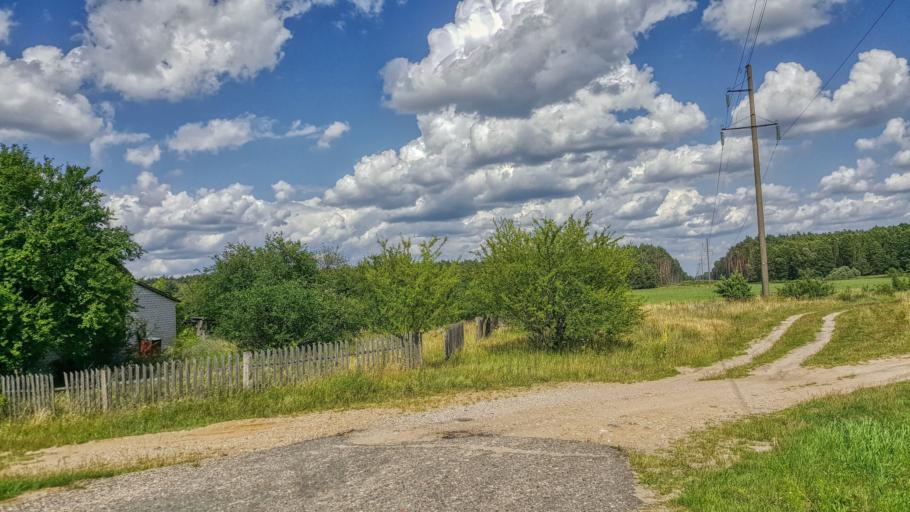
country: BY
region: Brest
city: Kamyanyets
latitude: 52.4134
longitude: 23.8899
